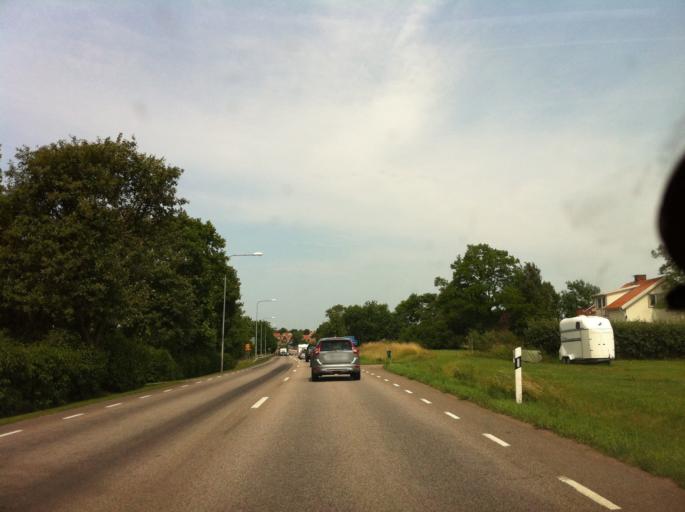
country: SE
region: Kalmar
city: Faerjestaden
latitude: 56.7139
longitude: 16.5326
